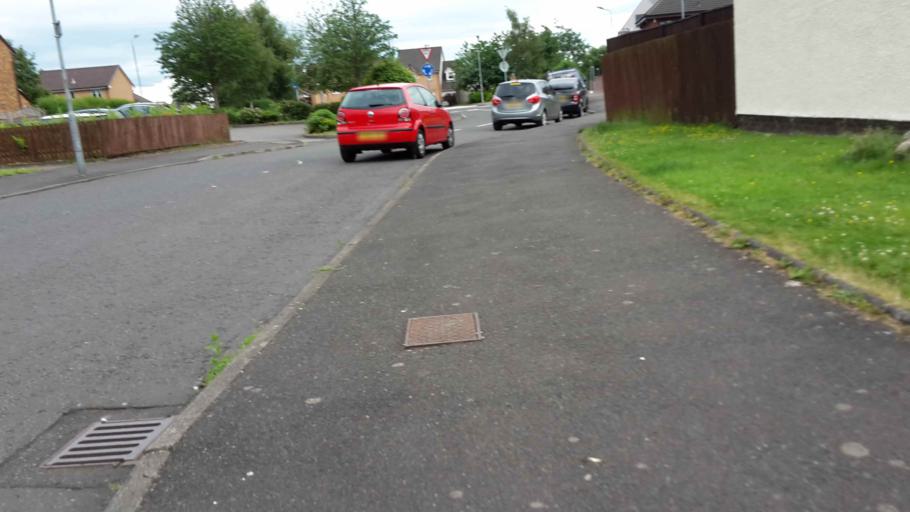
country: GB
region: Scotland
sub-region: South Lanarkshire
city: Uddingston
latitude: 55.8221
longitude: -4.0764
